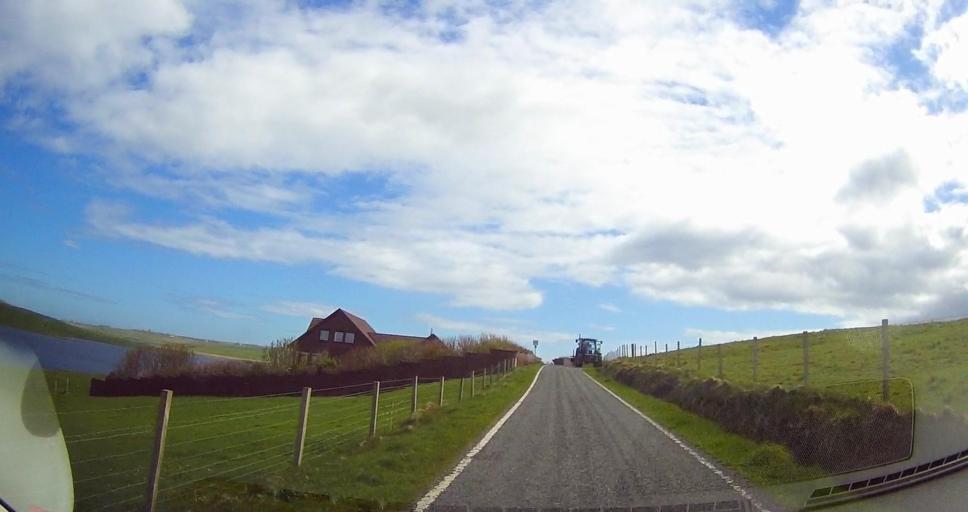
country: GB
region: Scotland
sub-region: Shetland Islands
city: Sandwick
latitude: 59.9319
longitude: -1.3457
